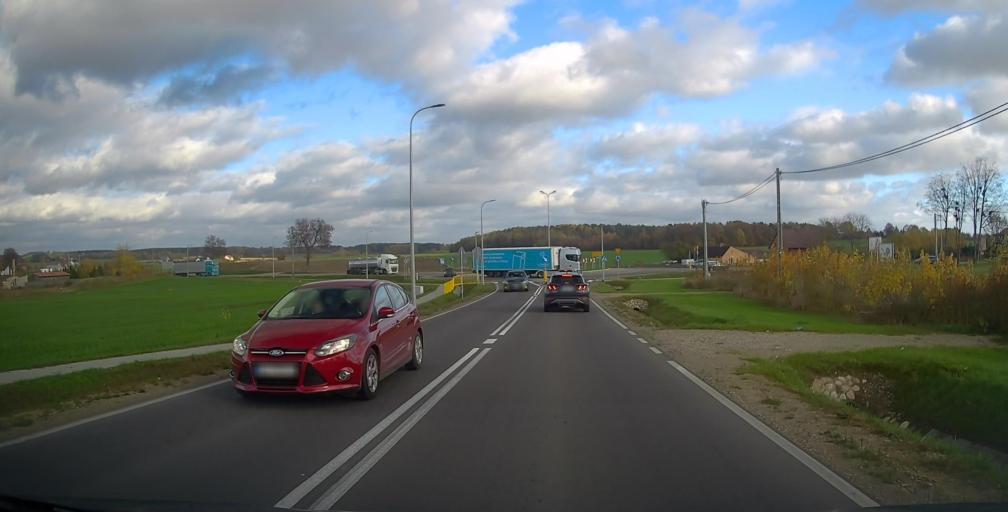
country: PL
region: Podlasie
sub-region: Powiat lomzynski
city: Piatnica
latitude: 53.2484
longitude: 22.1178
